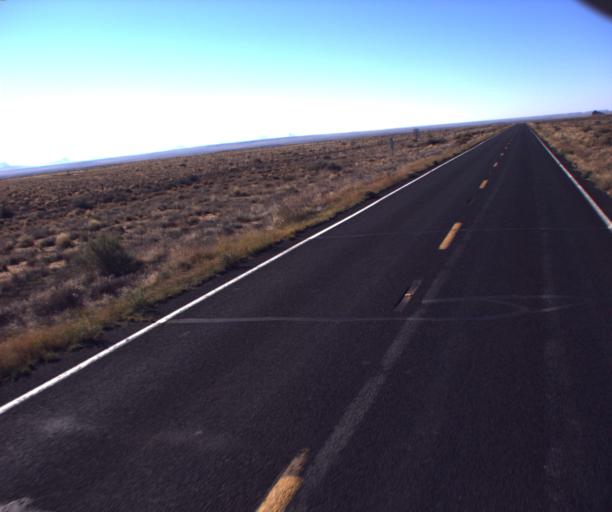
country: US
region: Arizona
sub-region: Navajo County
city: First Mesa
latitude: 35.7520
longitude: -110.5146
